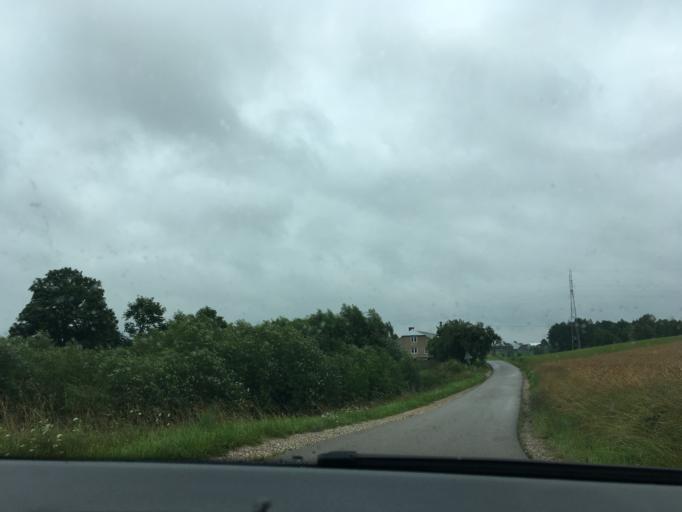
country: PL
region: Podlasie
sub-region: Powiat sejnenski
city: Sejny
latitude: 54.1034
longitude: 23.2802
